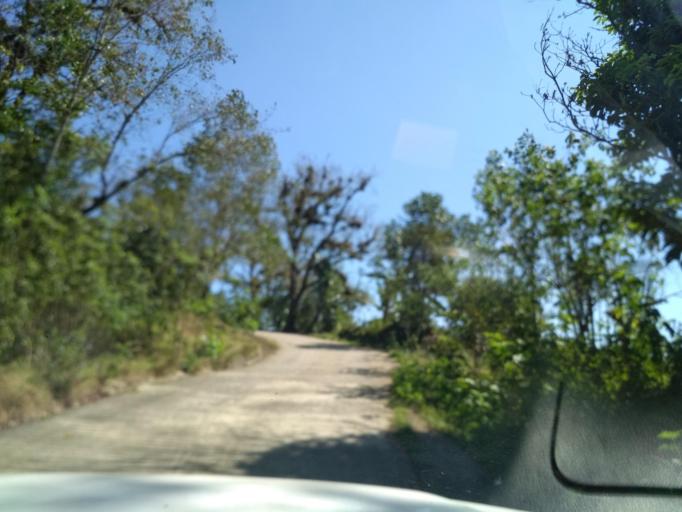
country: MX
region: Veracruz
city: Tequila
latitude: 18.7537
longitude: -97.0942
